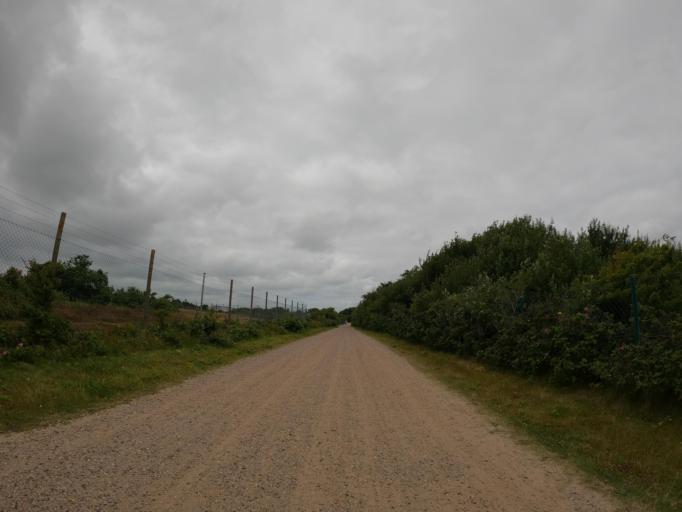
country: DE
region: Schleswig-Holstein
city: Tinnum
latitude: 54.9183
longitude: 8.3539
